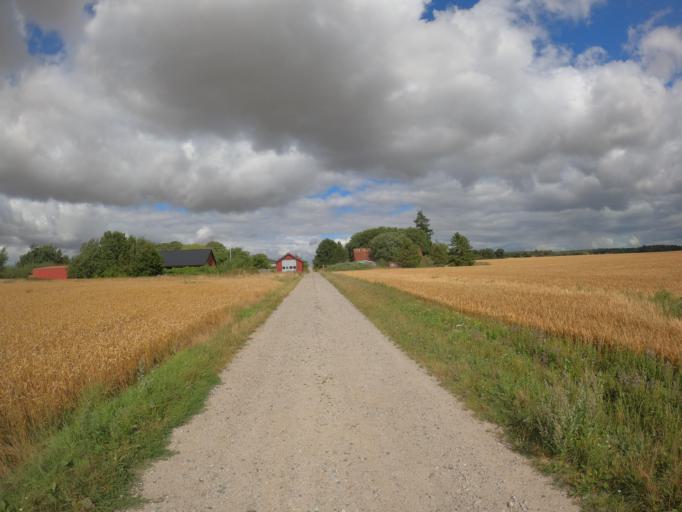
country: SE
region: Skane
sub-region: Lunds Kommun
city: Lund
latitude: 55.7297
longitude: 13.2730
